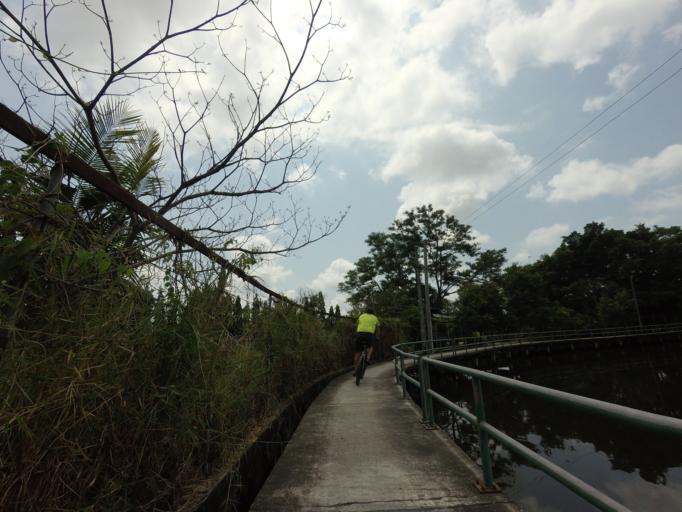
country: TH
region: Bangkok
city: Thung Khru
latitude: 13.6275
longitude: 100.4745
